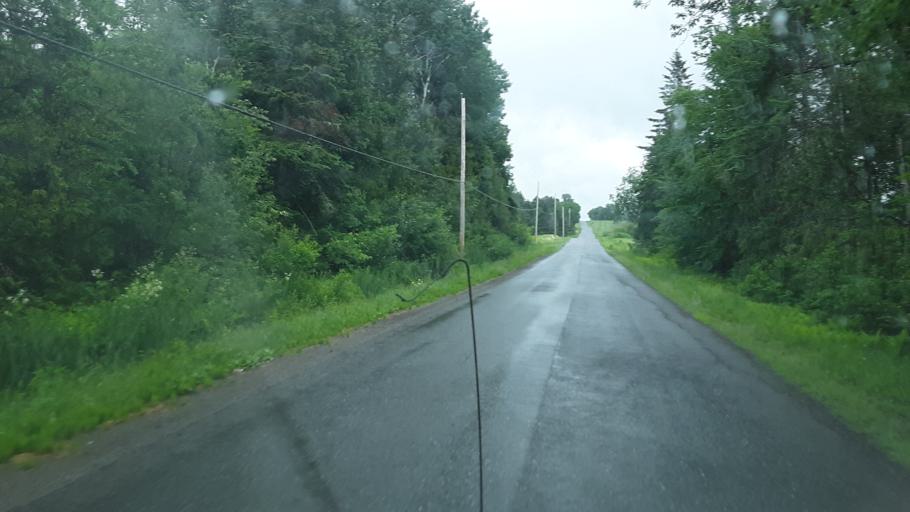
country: US
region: Maine
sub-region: Aroostook County
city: Presque Isle
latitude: 46.6816
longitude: -68.1983
